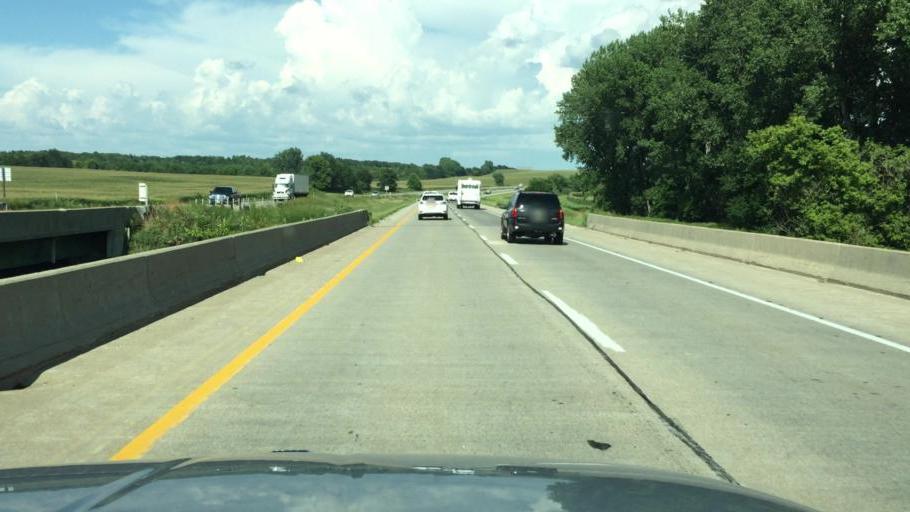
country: US
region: Iowa
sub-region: Poweshiek County
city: Grinnell
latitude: 41.6932
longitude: -92.8645
